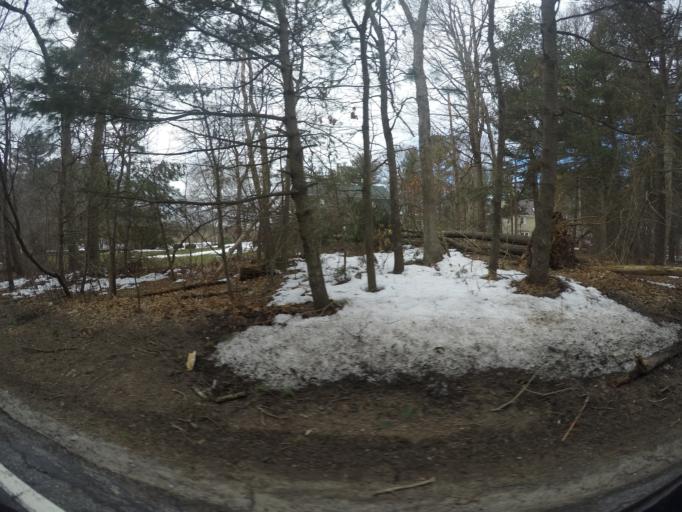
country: US
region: Massachusetts
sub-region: Bristol County
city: Easton
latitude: 42.0548
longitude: -71.1305
